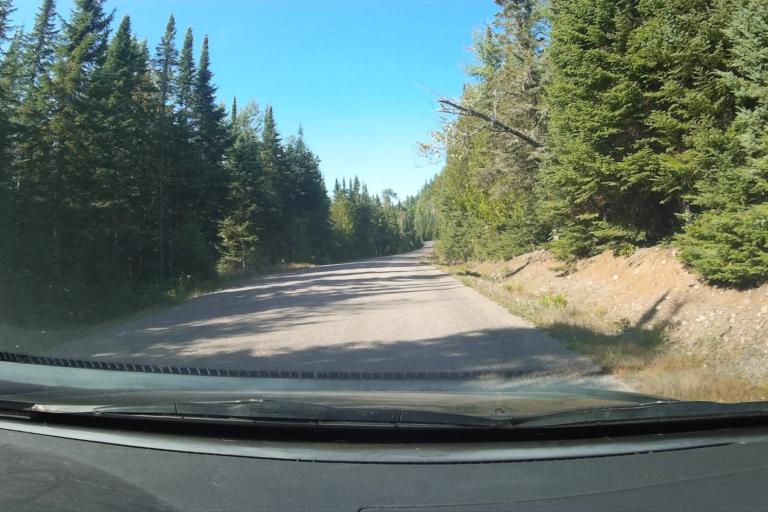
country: CA
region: Ontario
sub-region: Thunder Bay District
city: Thunder Bay
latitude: 48.3442
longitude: -88.8132
